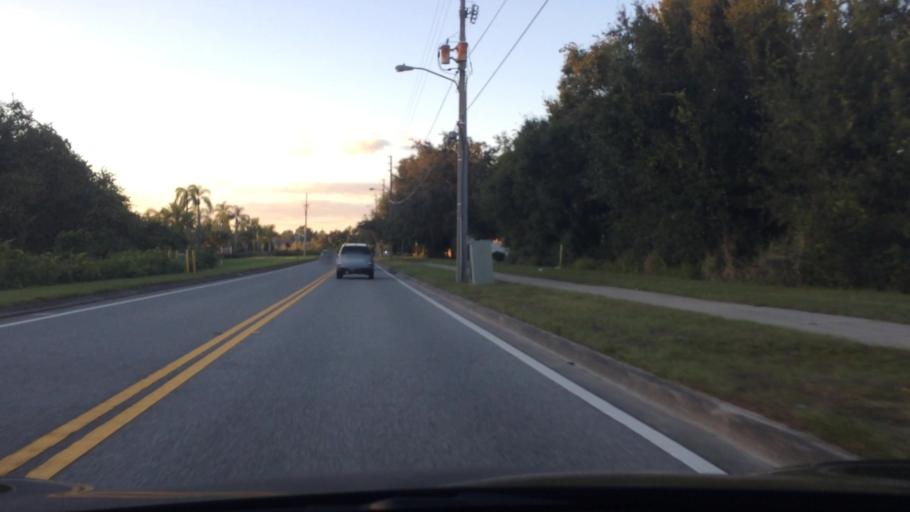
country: US
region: Florida
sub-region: Hillsborough County
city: Lutz
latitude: 28.1754
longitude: -82.4383
